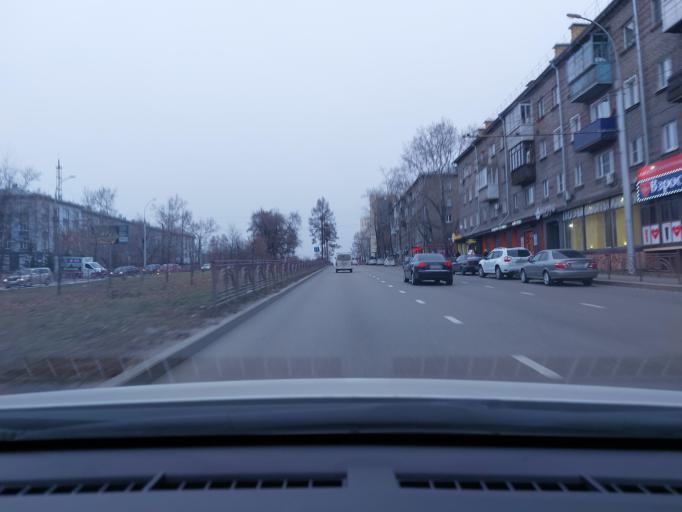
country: RU
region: Irkutsk
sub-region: Irkutskiy Rayon
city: Irkutsk
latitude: 52.2648
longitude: 104.2587
